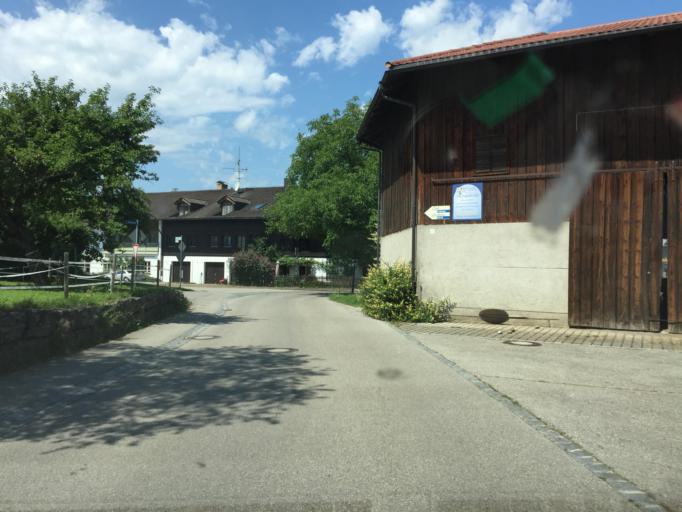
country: DE
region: Bavaria
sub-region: Upper Bavaria
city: Tuntenhausen
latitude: 47.9348
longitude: 12.0169
